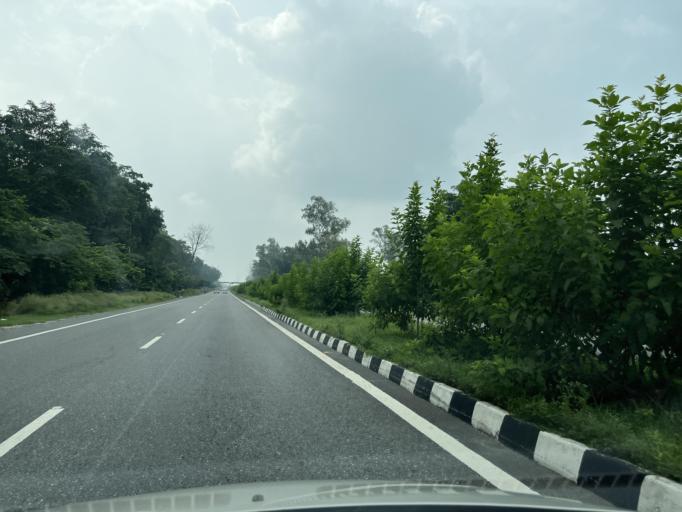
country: IN
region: Uttarakhand
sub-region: Dehradun
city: Doiwala
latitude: 30.1100
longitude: 78.1710
